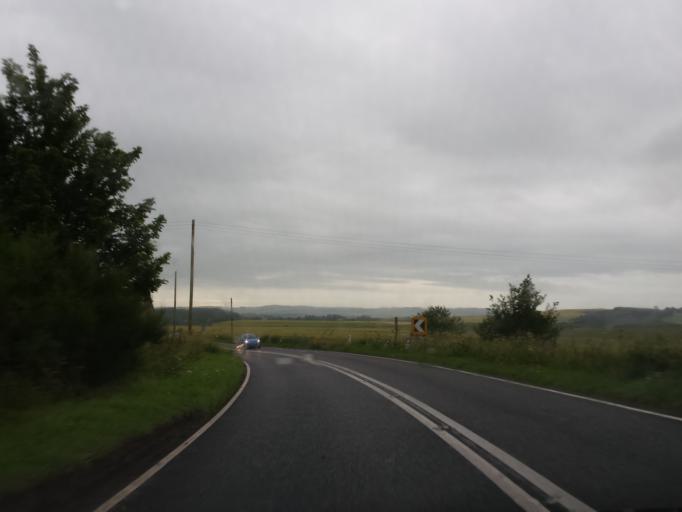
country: GB
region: Scotland
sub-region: Fife
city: Balmullo
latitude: 56.4058
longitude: -2.9155
